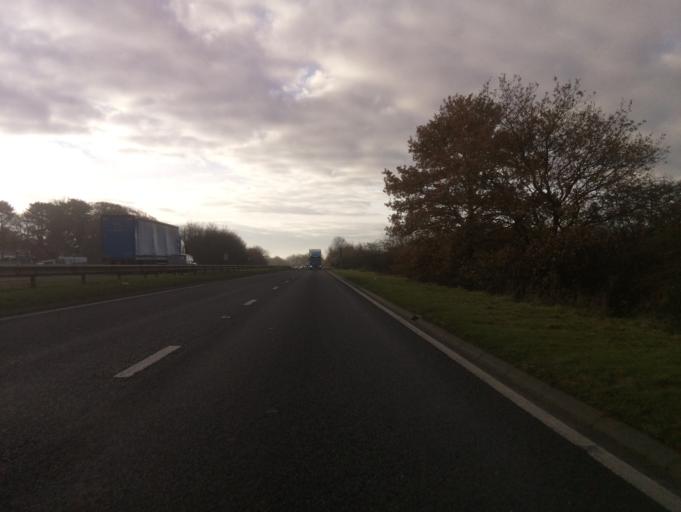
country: GB
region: England
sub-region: City and Borough of Birmingham
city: Sutton Coldfield
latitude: 52.6033
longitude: -1.7958
